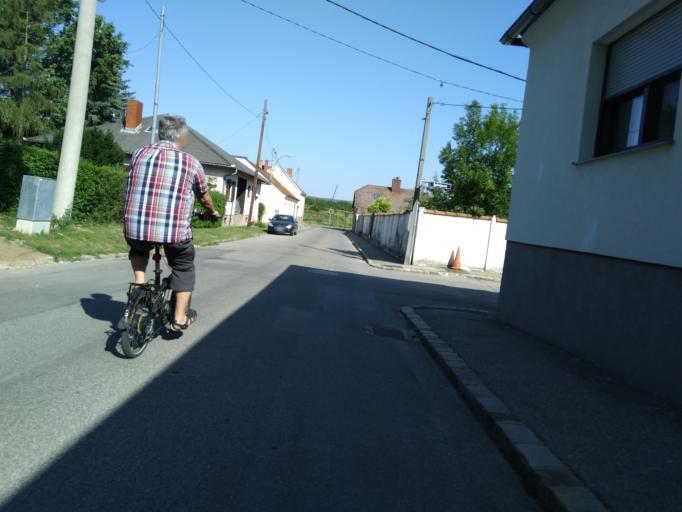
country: AT
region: Lower Austria
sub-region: Politischer Bezirk Mistelbach
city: Wolkersdorf im Weinviertel
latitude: 48.3835
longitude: 16.5086
